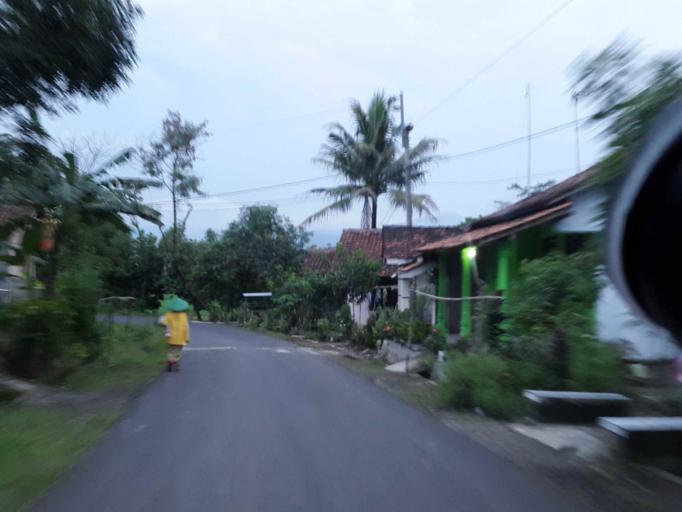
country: ID
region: Central Java
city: Randudongkal
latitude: -7.0845
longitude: 109.3438
